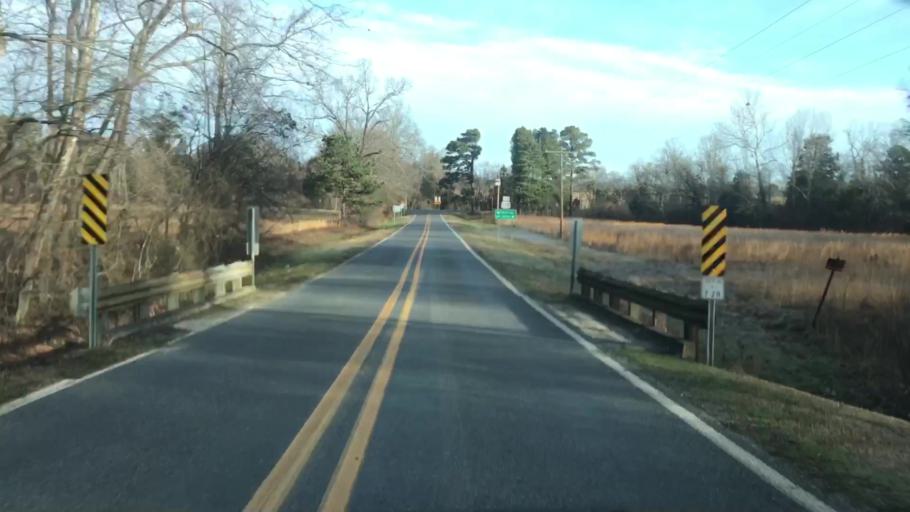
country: US
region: Arkansas
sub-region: Garland County
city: Rockwell
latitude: 34.5086
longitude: -93.2761
